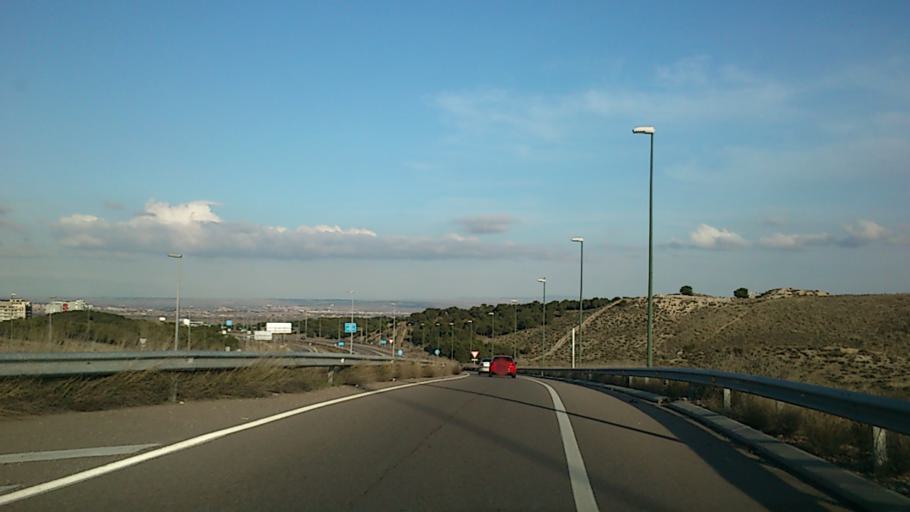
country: ES
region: Aragon
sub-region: Provincia de Zaragoza
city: Zaragoza
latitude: 41.6074
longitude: -0.8786
